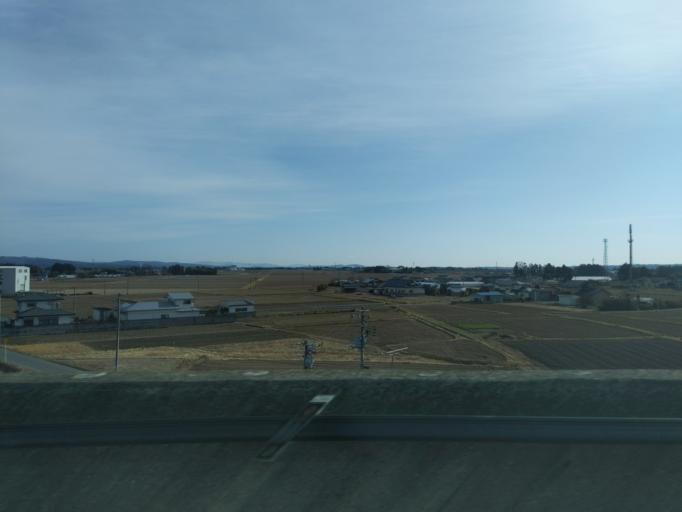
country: JP
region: Miyagi
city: Furukawa
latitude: 38.5904
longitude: 140.9755
